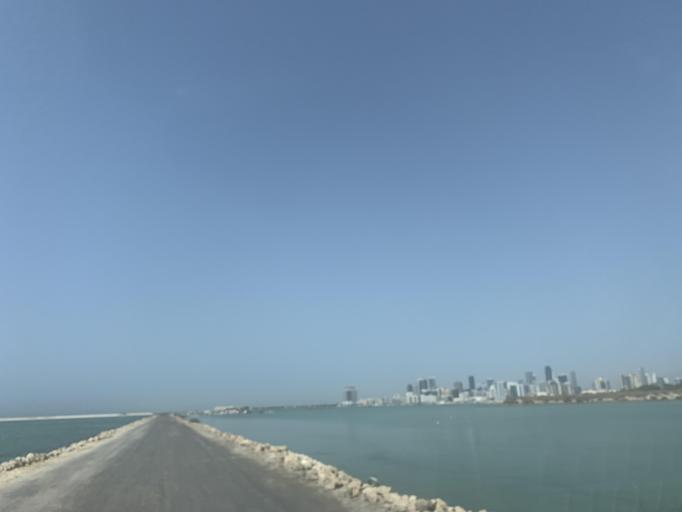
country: BH
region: Manama
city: Jidd Hafs
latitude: 26.2365
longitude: 50.5103
